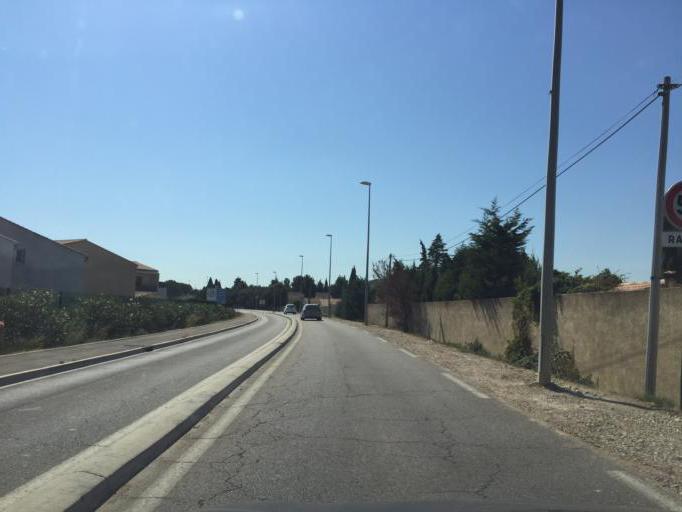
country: FR
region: Provence-Alpes-Cote d'Azur
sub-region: Departement du Vaucluse
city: Vedene
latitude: 43.9756
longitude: 4.9097
